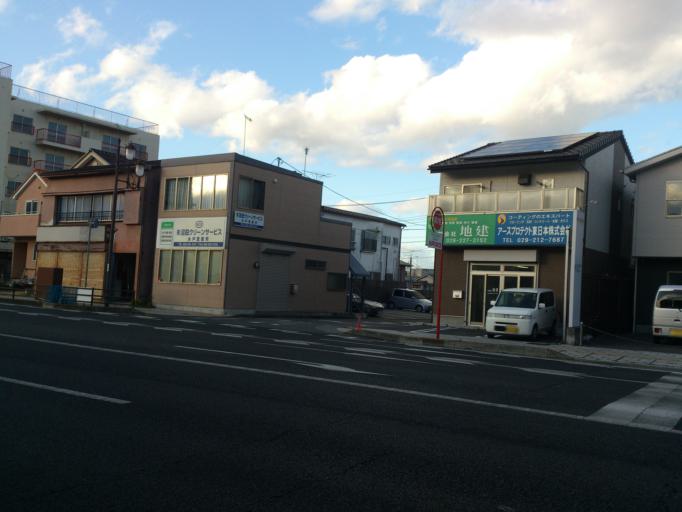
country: JP
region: Ibaraki
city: Mito-shi
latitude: 36.3813
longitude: 140.4553
